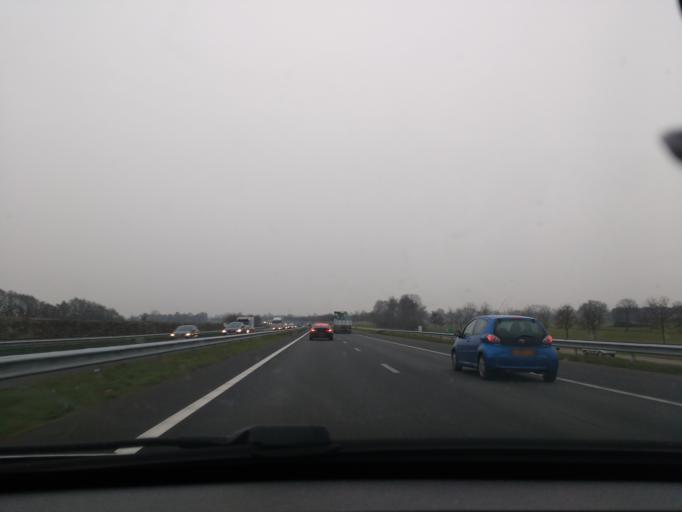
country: NL
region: Gelderland
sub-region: Gemeente Ede
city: Lunteren
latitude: 52.0861
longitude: 5.5964
